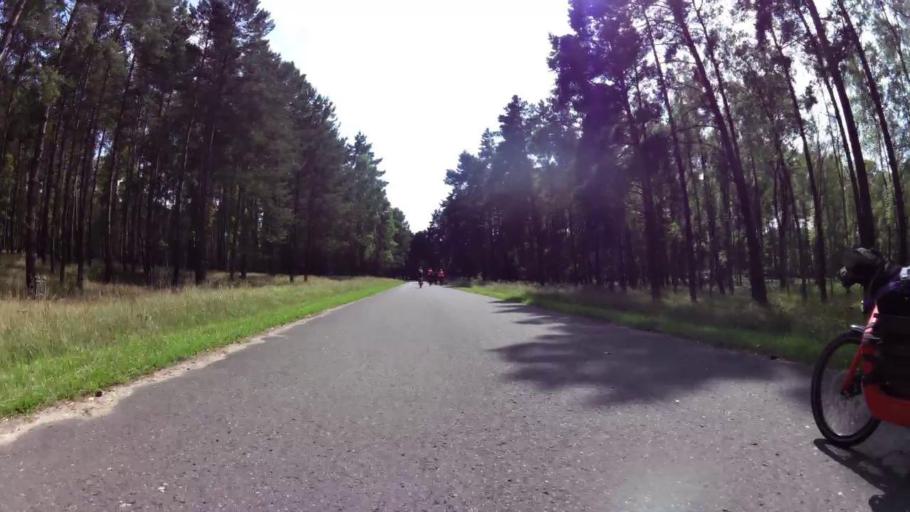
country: PL
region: West Pomeranian Voivodeship
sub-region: Powiat choszczenski
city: Drawno
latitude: 53.3539
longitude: 15.7021
